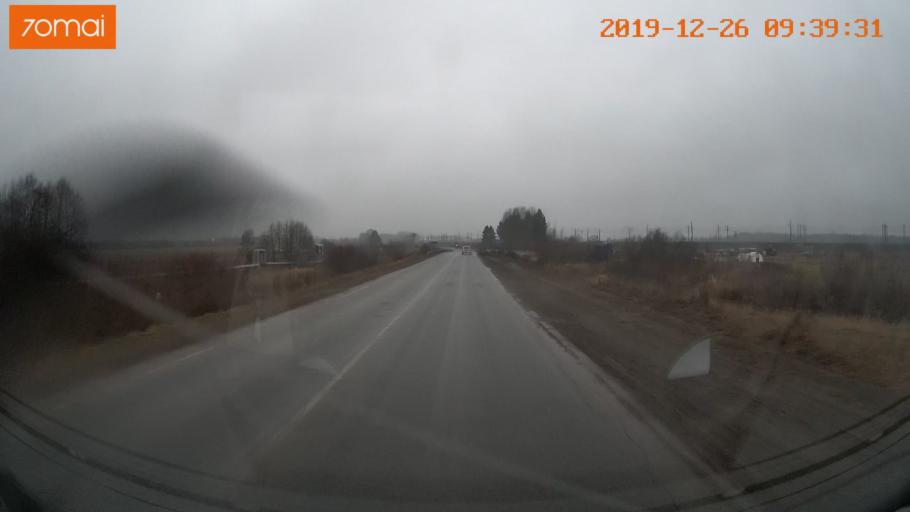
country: RU
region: Vologda
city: Vologda
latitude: 59.1557
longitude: 40.0235
